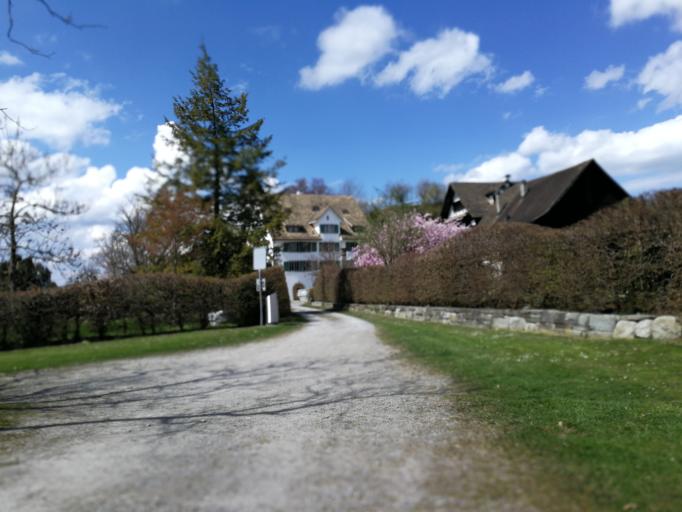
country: CH
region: Zurich
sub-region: Bezirk Meilen
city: Hombrechtikon
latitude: 47.2338
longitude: 8.7782
